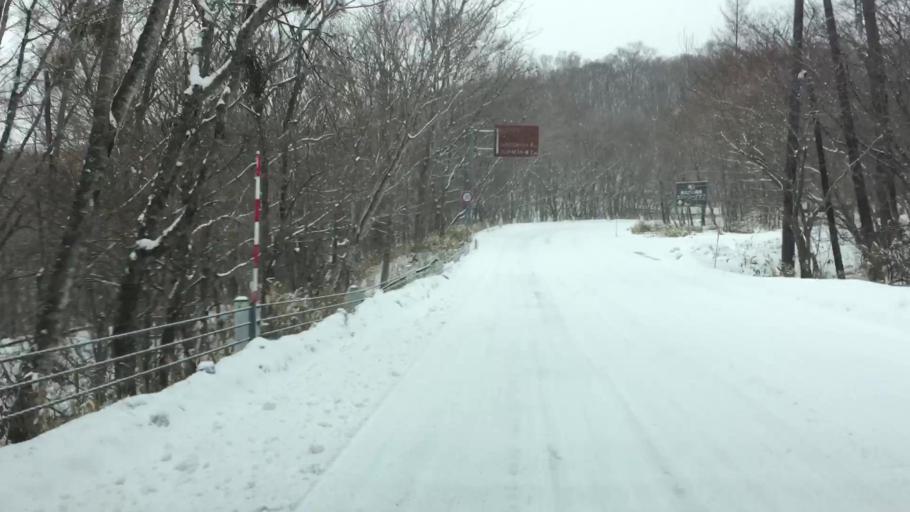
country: JP
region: Tochigi
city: Imaichi
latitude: 36.8965
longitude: 139.7393
